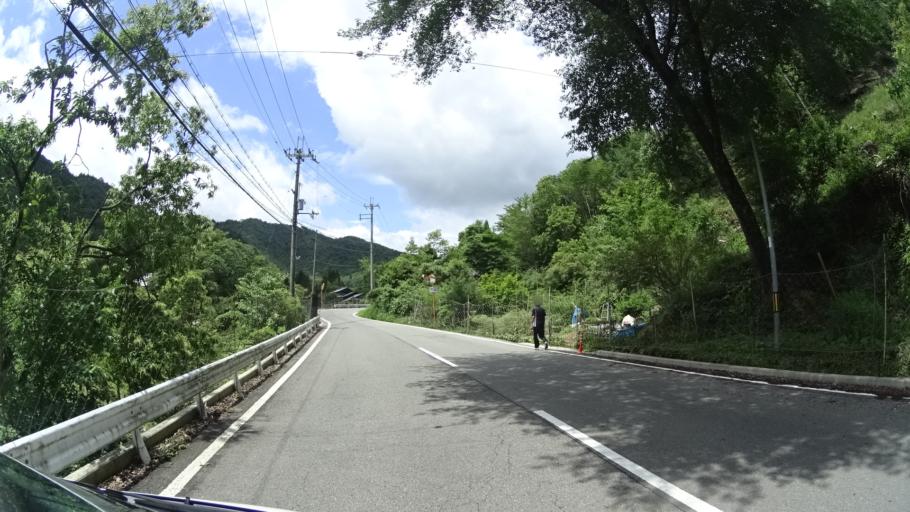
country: JP
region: Kyoto
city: Kameoka
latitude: 35.0217
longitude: 135.3996
